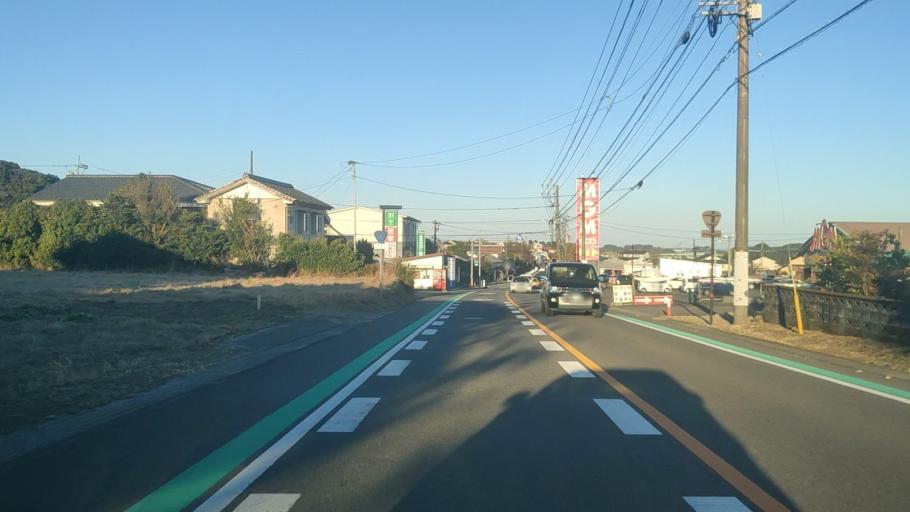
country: JP
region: Miyazaki
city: Miyazaki-shi
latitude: 31.8422
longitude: 131.3403
